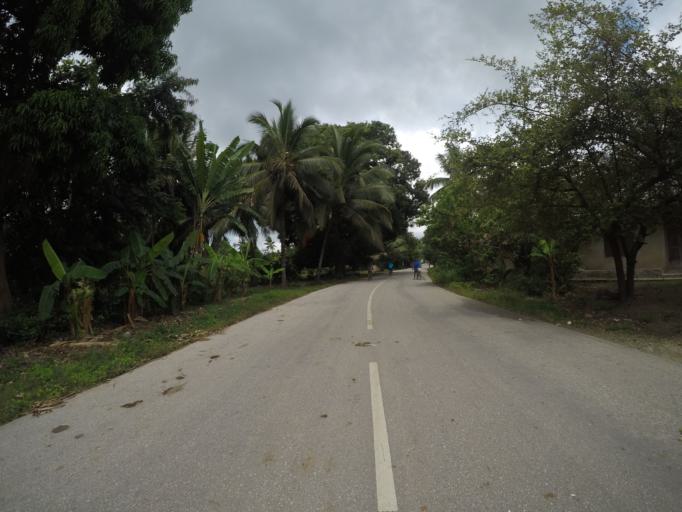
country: TZ
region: Pemba South
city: Mtambile
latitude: -5.3866
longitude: 39.7457
